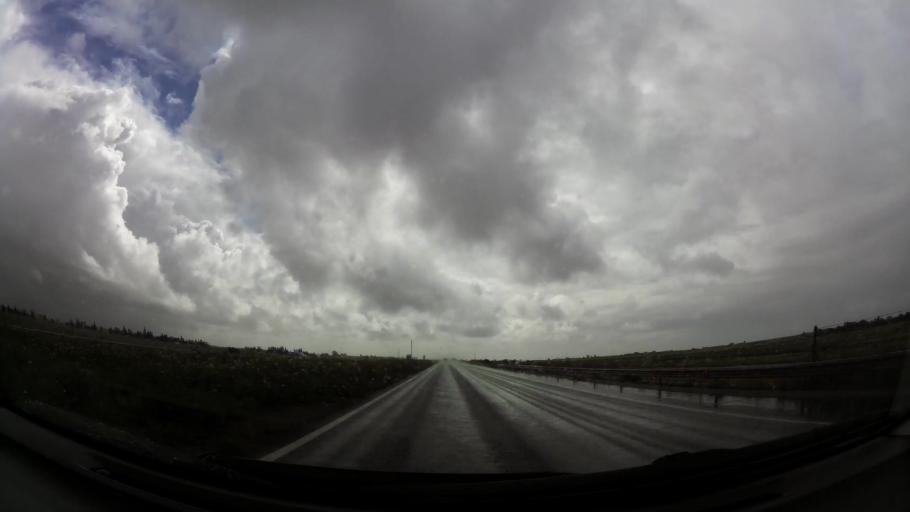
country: MA
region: Grand Casablanca
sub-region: Nouaceur
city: Dar Bouazza
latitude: 33.3939
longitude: -7.8556
